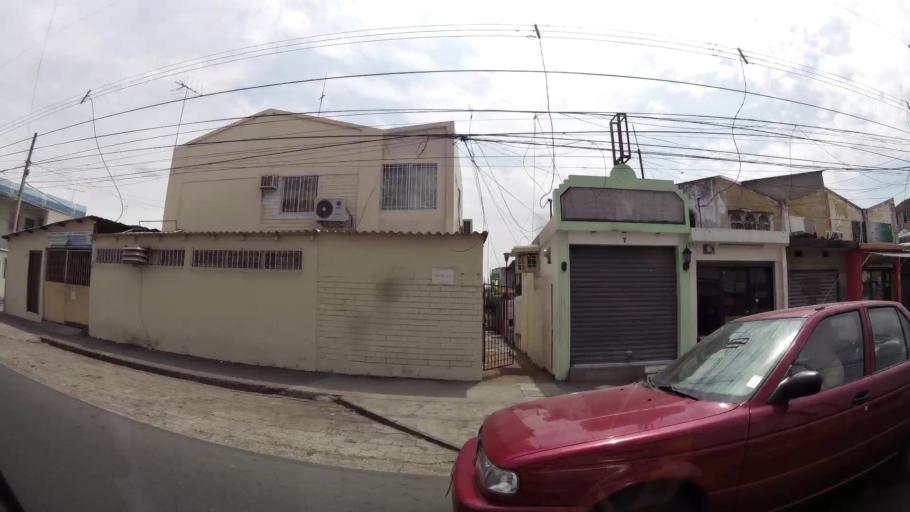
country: EC
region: Guayas
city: Eloy Alfaro
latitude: -2.1412
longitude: -79.9008
